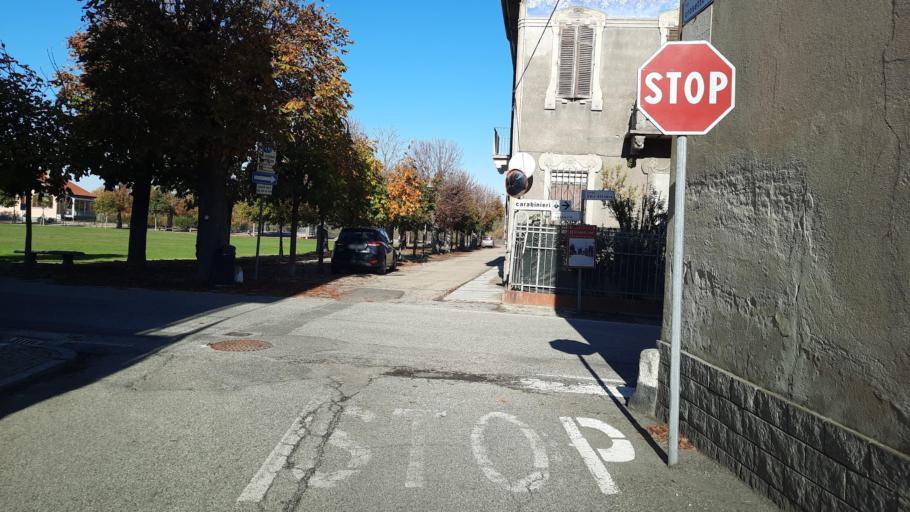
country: IT
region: Piedmont
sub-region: Provincia di Alessandria
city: Pontestura
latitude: 45.1437
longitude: 8.3347
